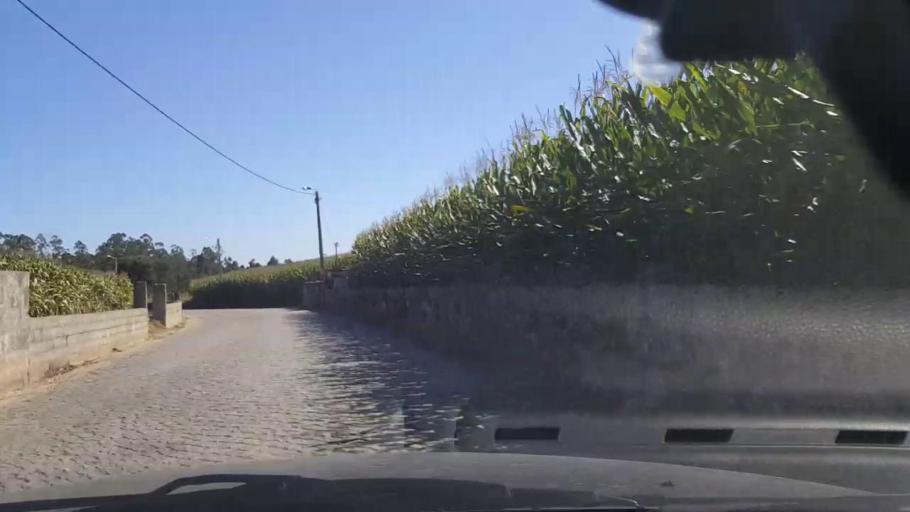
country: PT
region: Porto
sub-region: Vila do Conde
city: Arvore
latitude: 41.3170
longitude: -8.6917
